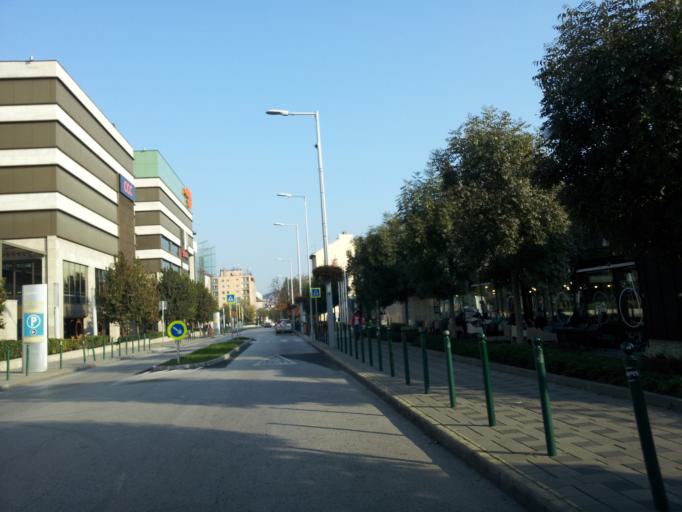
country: HU
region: Budapest
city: Budapest XII. keruelet
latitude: 47.4902
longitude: 19.0220
